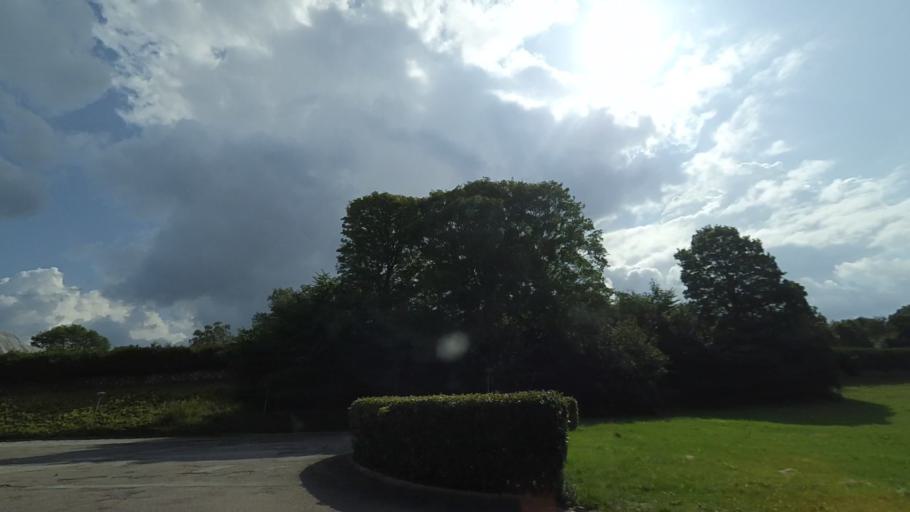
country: DK
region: Central Jutland
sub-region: Norddjurs Kommune
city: Allingabro
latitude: 56.4977
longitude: 10.3369
